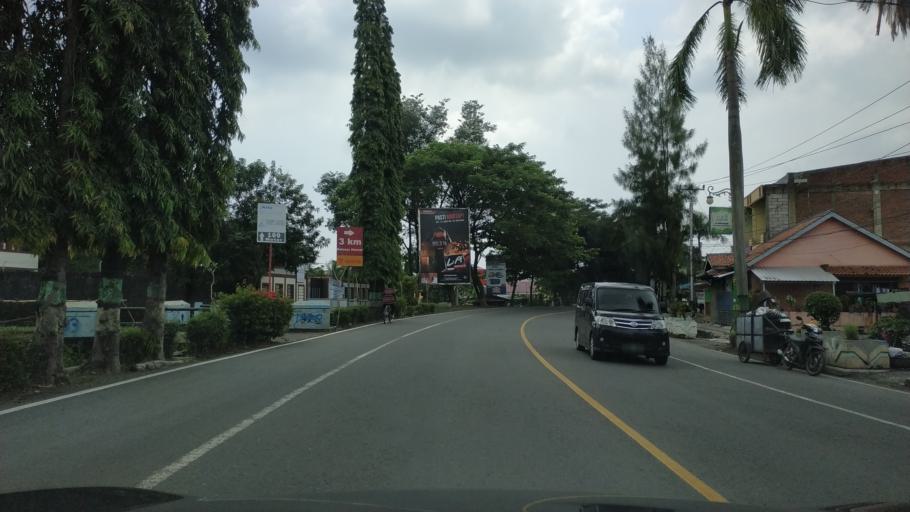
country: ID
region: Central Java
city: Slawi
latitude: -6.9985
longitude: 109.1407
